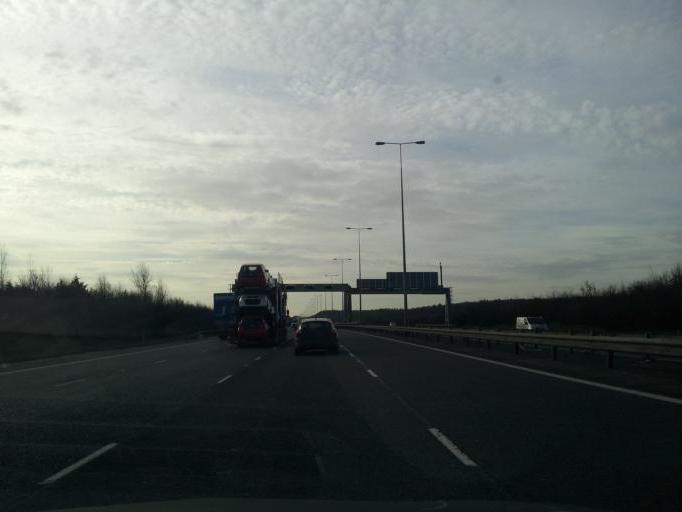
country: GB
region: England
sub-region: Cambridgeshire
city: Sawtry
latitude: 52.4186
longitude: -0.2676
